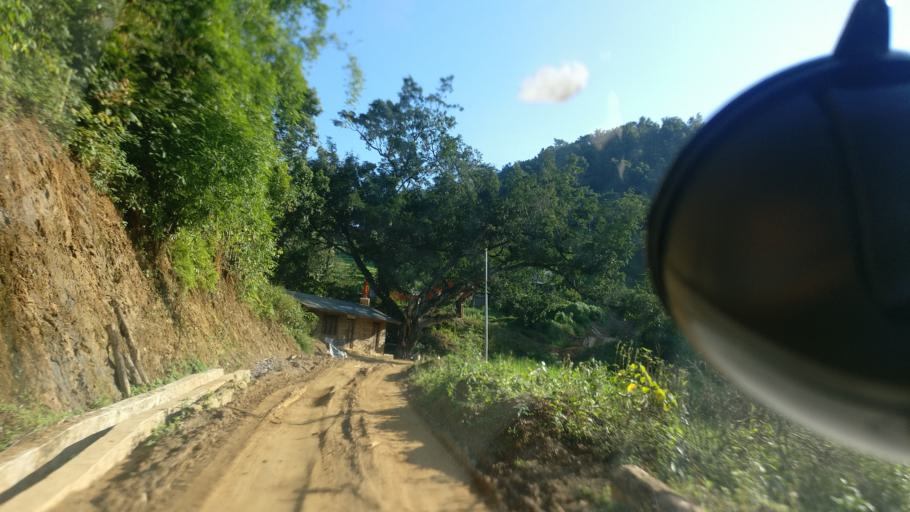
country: NP
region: Western Region
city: Baglung
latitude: 28.1524
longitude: 83.6547
